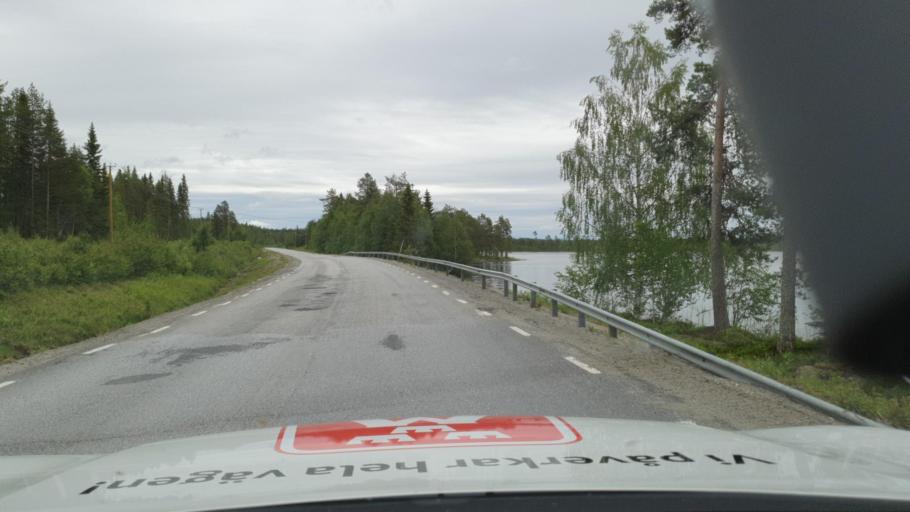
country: SE
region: Vaesterbotten
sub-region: Lycksele Kommun
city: Lycksele
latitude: 64.0907
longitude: 18.3779
